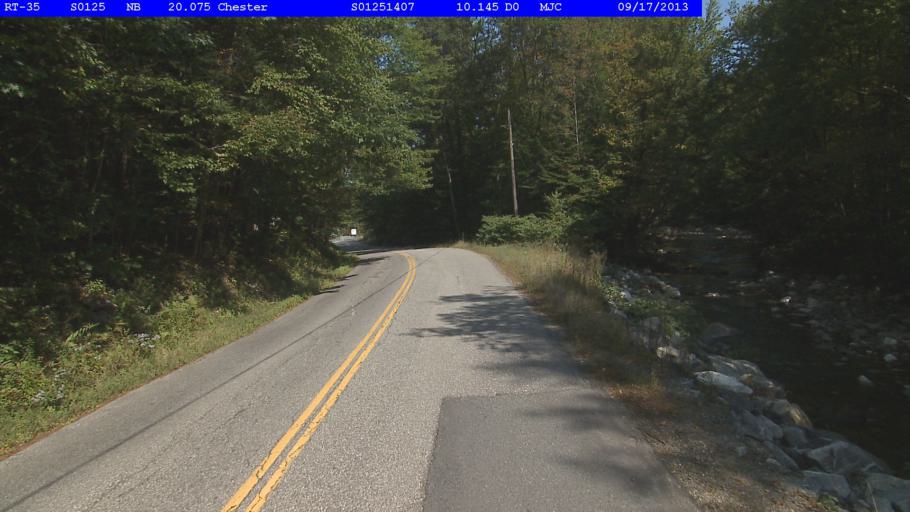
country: US
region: Vermont
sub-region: Windsor County
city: Chester
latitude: 43.2496
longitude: -72.6037
